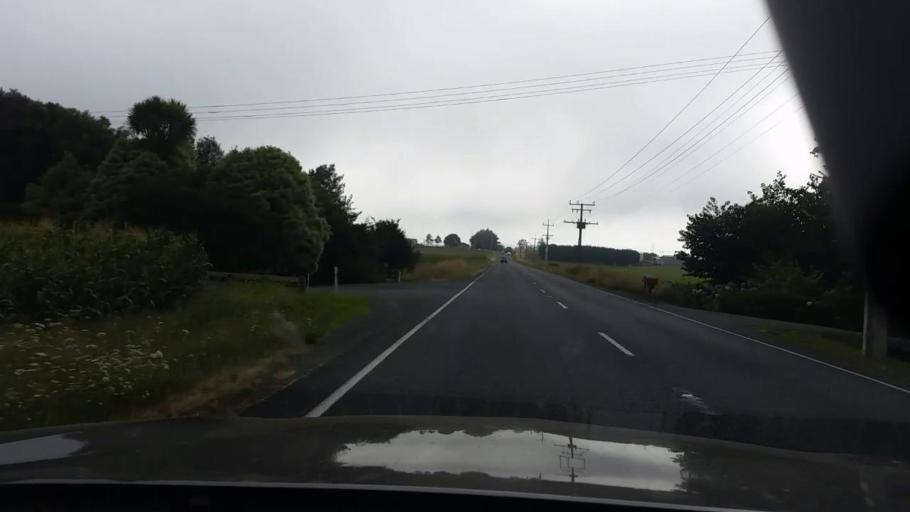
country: NZ
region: Waikato
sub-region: Hamilton City
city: Hamilton
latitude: -37.6231
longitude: 175.3281
